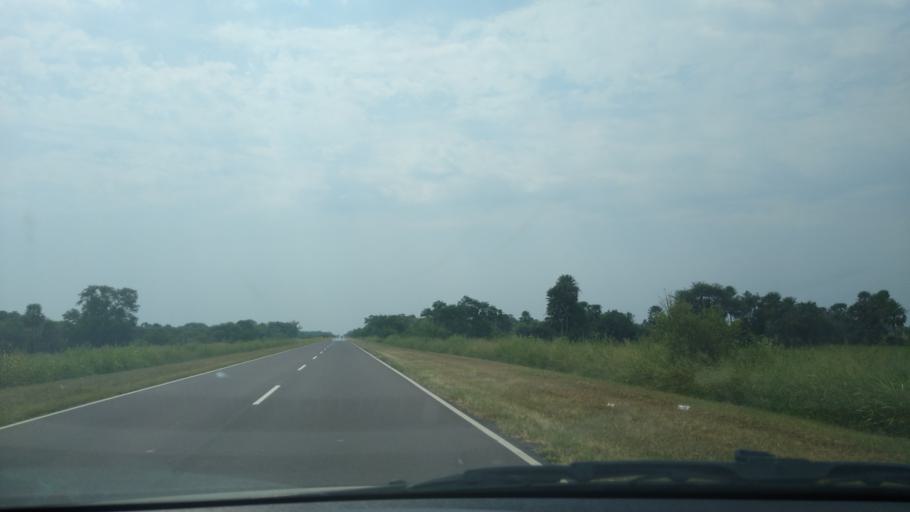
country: AR
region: Chaco
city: La Eduvigis
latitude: -27.0300
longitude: -58.9661
